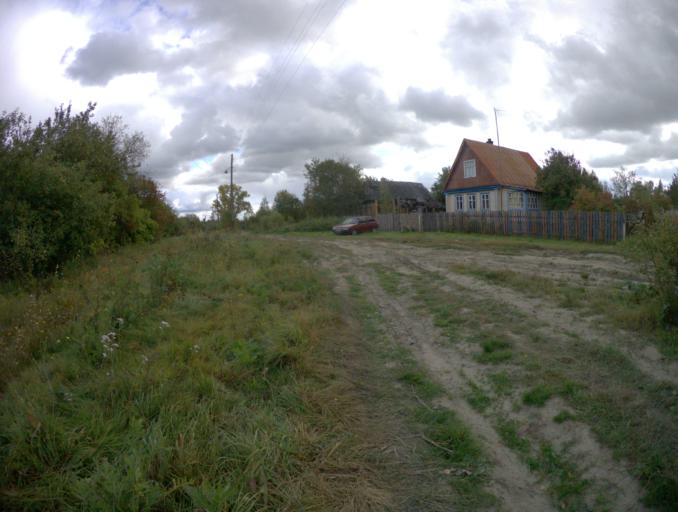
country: RU
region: Vladimir
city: Urshel'skiy
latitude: 55.7848
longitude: 40.1638
